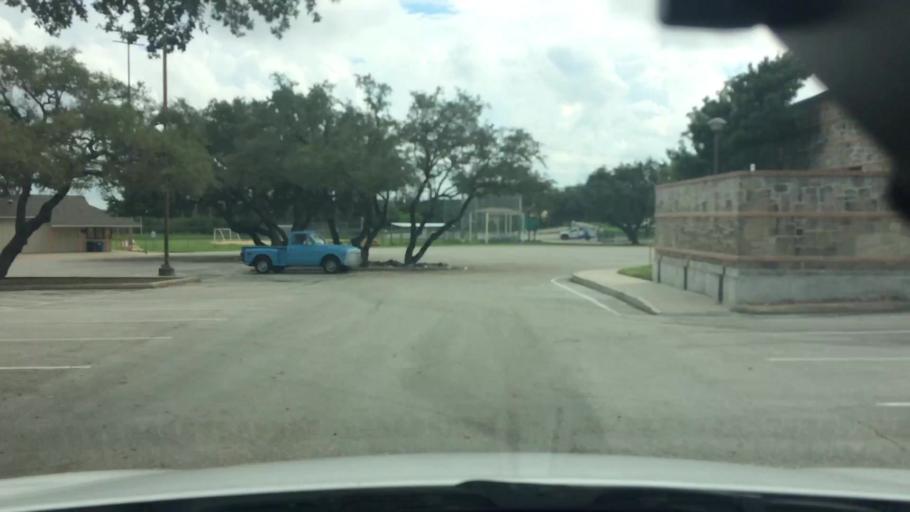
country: US
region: Texas
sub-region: Bexar County
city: Shavano Park
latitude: 29.5764
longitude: -98.5681
